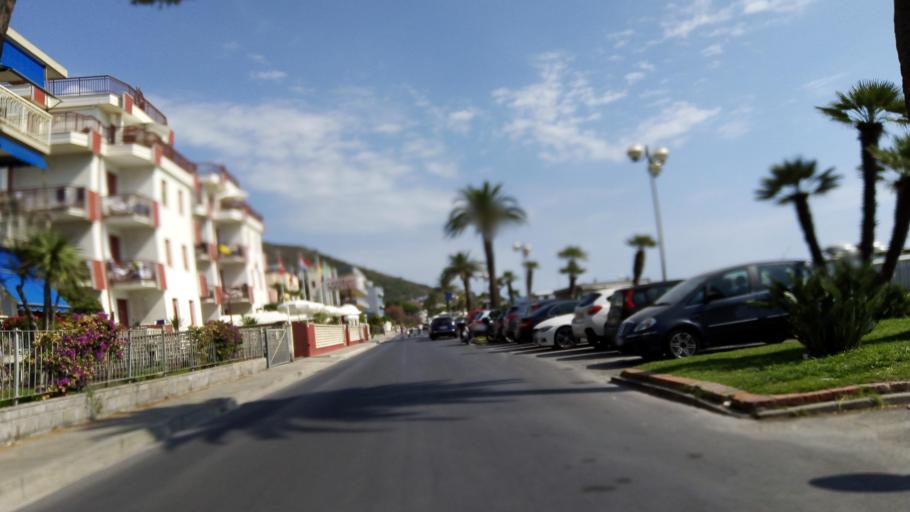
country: IT
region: Liguria
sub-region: Provincia di Savona
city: Ceriale
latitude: 44.0900
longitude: 8.2302
